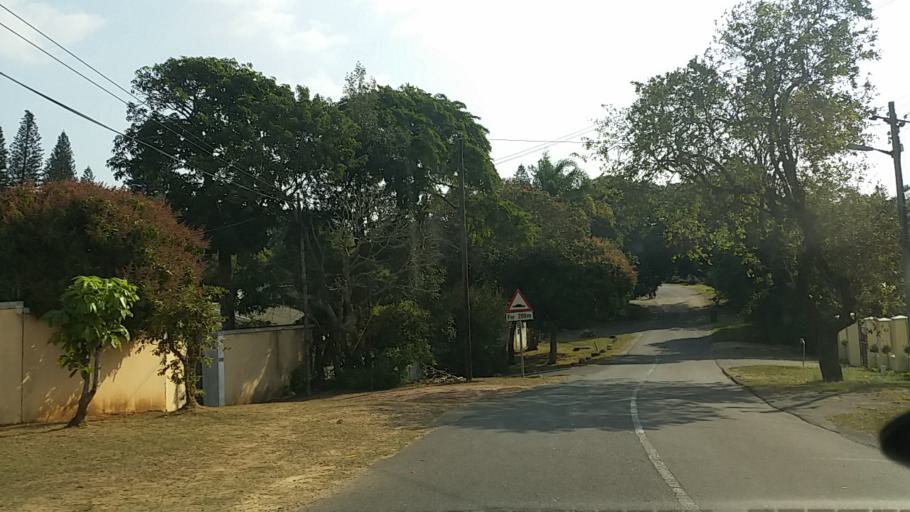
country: ZA
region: KwaZulu-Natal
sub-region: eThekwini Metropolitan Municipality
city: Berea
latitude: -29.8392
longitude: 30.9428
